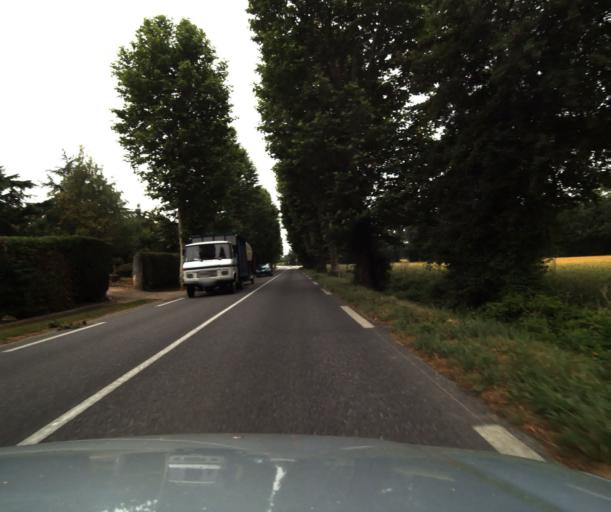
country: FR
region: Midi-Pyrenees
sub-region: Departement du Gers
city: Gimont
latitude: 43.7256
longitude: 0.8751
